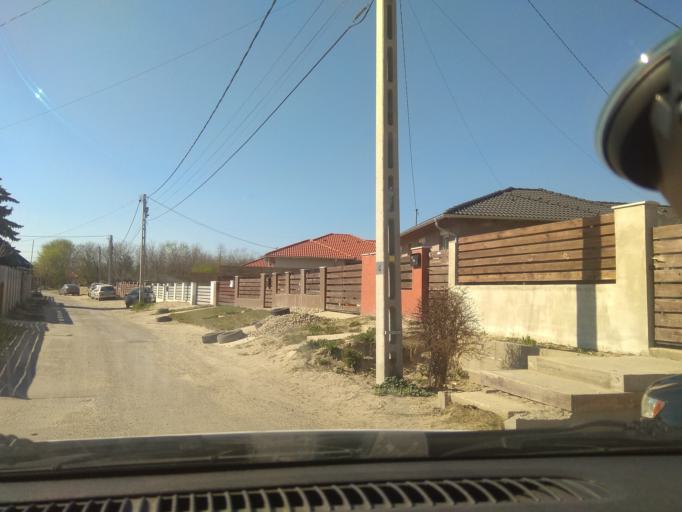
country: HU
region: Pest
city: Szigethalom
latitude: 47.3221
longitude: 19.0201
